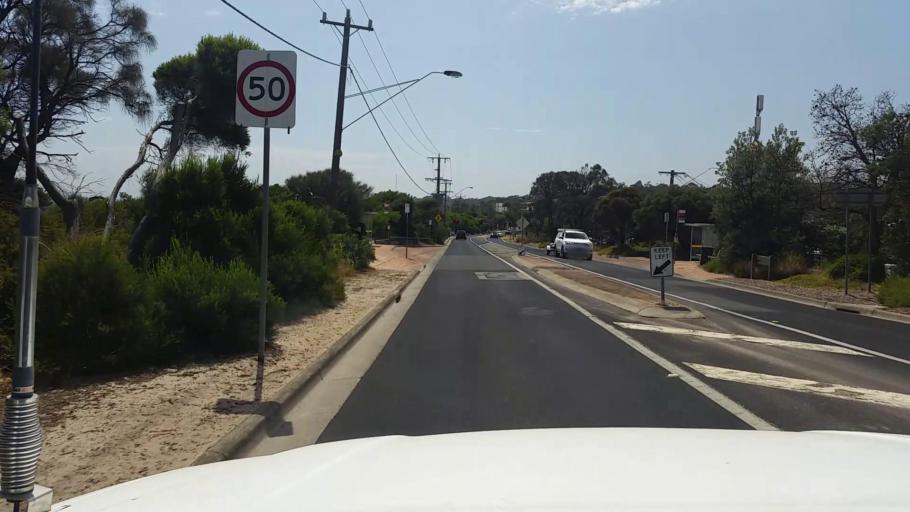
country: AU
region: Victoria
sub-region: Mornington Peninsula
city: Mount Martha
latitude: -38.2678
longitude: 145.0123
